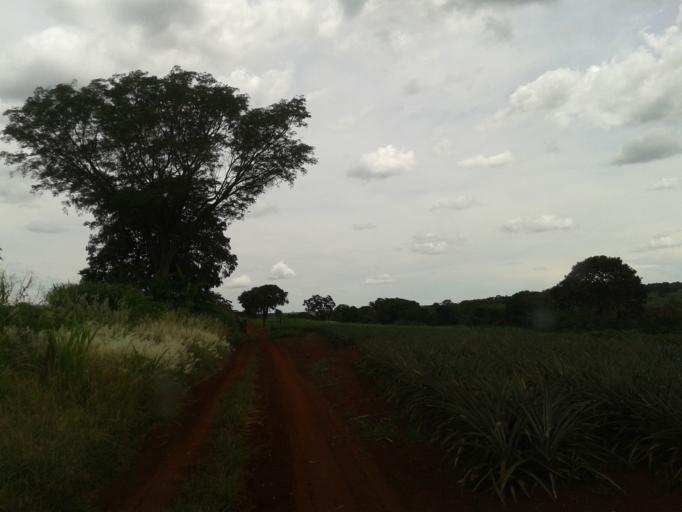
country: BR
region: Minas Gerais
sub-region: Centralina
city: Centralina
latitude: -18.6791
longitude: -49.2365
